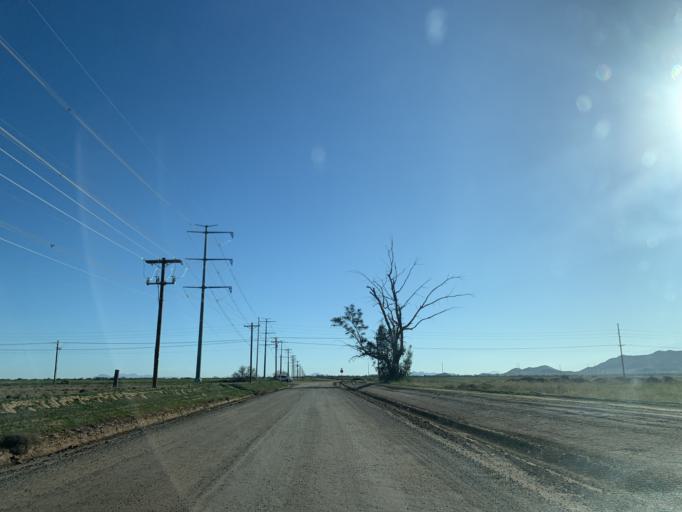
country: US
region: Arizona
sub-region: Pinal County
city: Casa Grande
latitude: 32.8518
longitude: -111.6711
